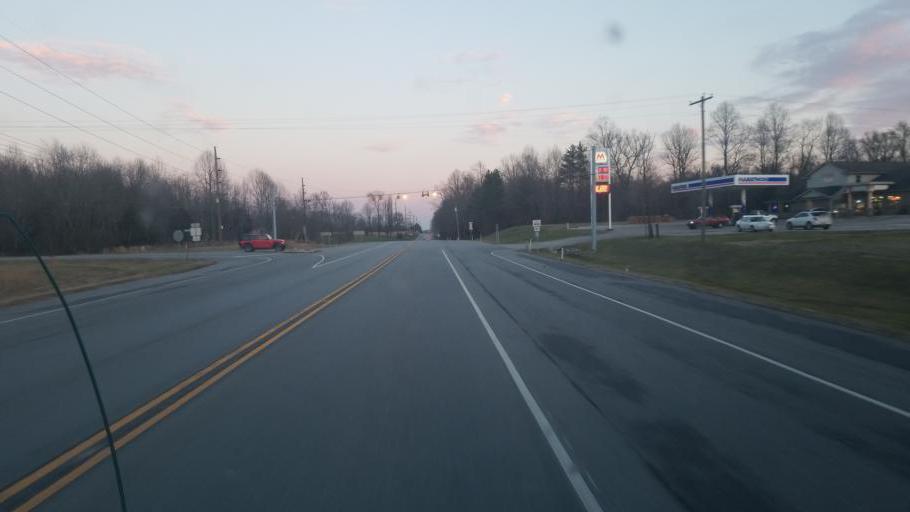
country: US
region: Indiana
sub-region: Lawrence County
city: Bedford
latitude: 38.8746
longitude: -86.3405
